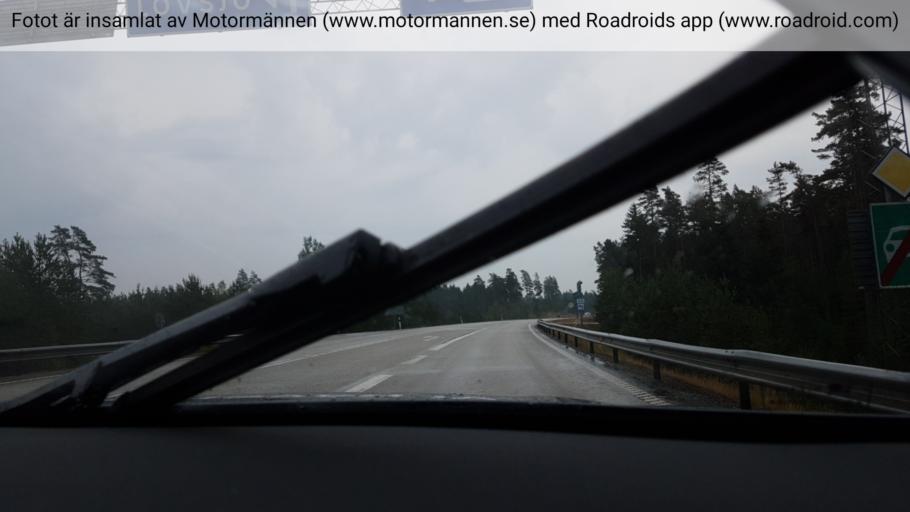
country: SE
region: Joenkoeping
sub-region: Jonkopings Kommun
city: Odensjo
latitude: 57.6169
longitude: 14.2014
